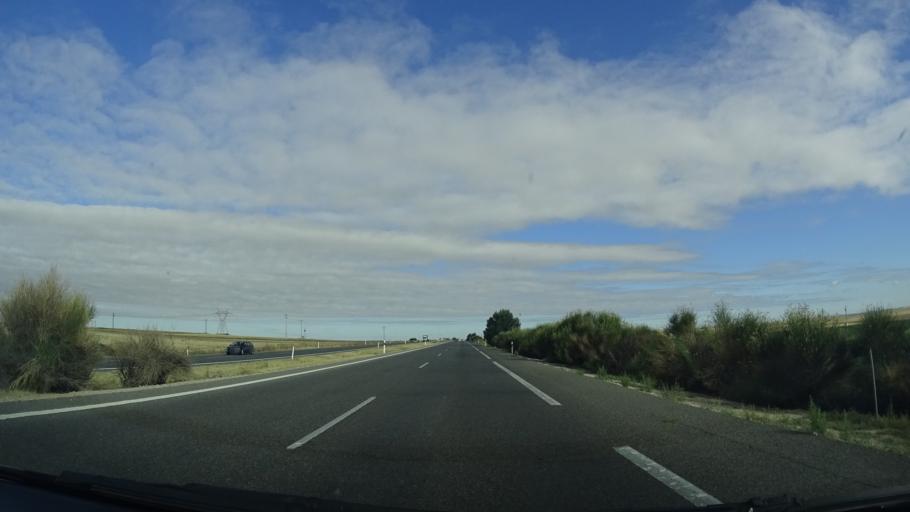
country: ES
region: Castille and Leon
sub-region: Provincia de Valladolid
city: Ataquines
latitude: 41.1956
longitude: -4.8175
